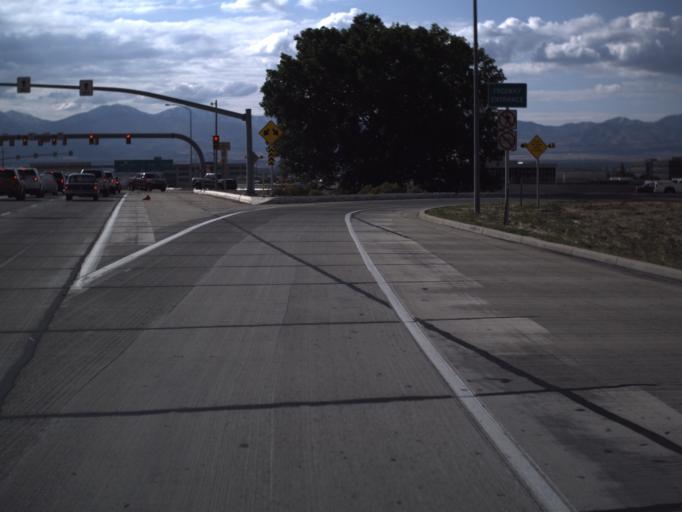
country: US
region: Utah
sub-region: Salt Lake County
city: Draper
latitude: 40.5046
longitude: -111.8898
